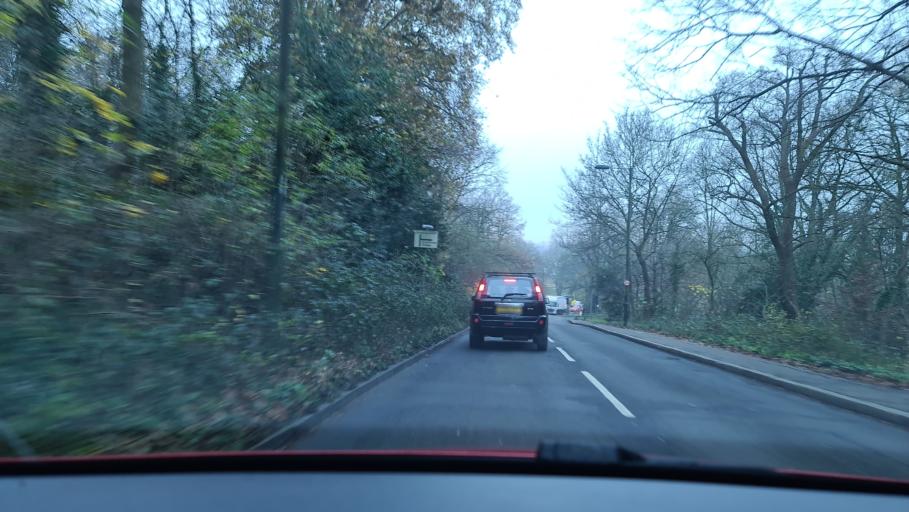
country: GB
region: England
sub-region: Greater London
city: Richmond
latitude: 51.4477
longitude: -0.2976
